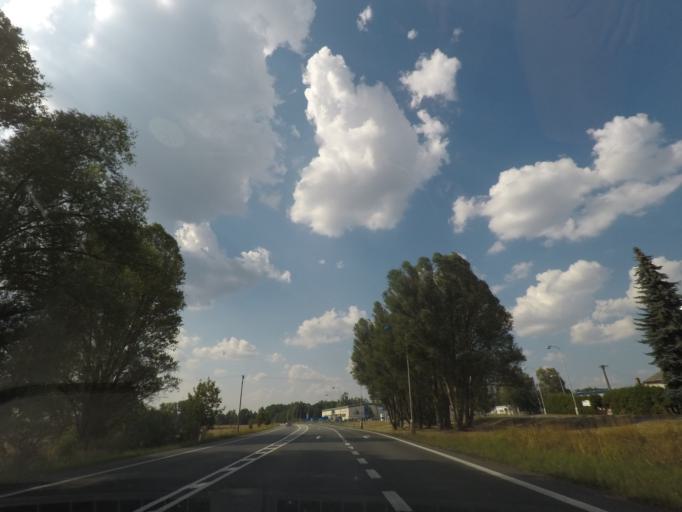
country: CZ
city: Tyniste nad Orlici
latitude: 50.1565
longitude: 16.0649
